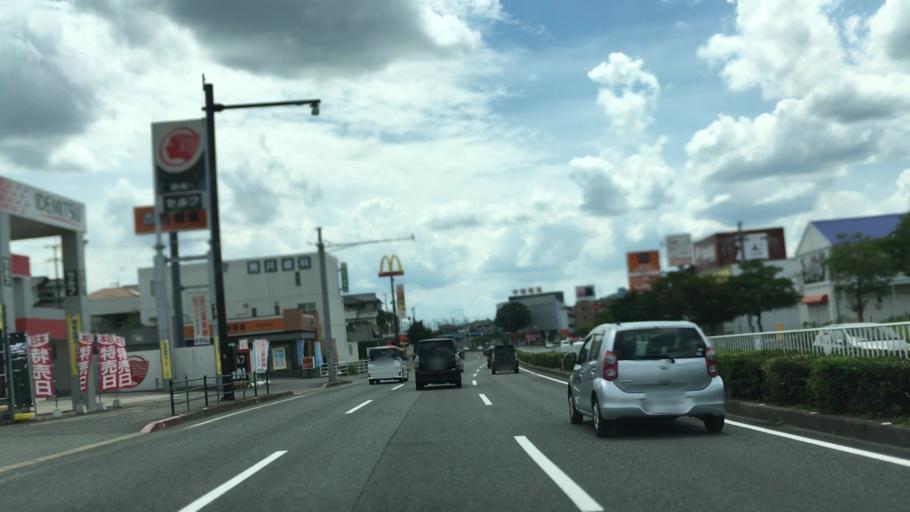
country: JP
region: Fukuoka
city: Dazaifu
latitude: 33.5024
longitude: 130.5313
